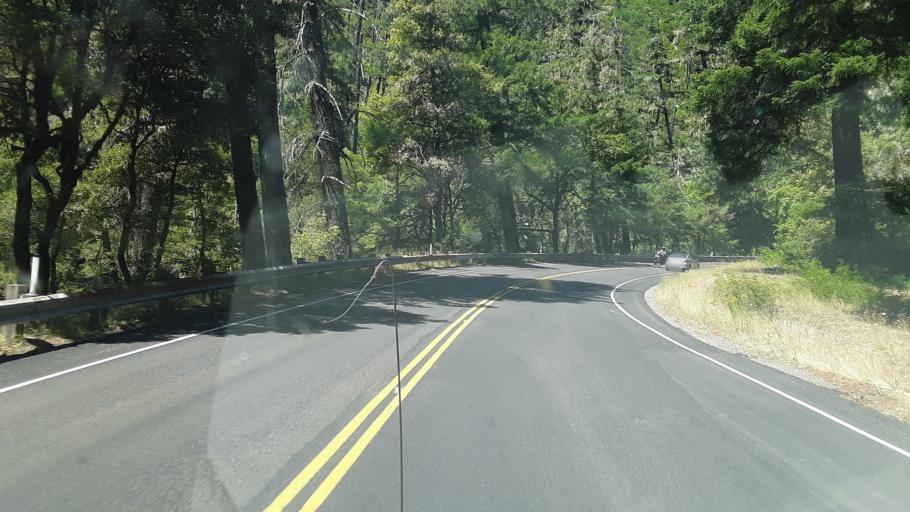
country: US
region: Oregon
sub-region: Josephine County
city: Cave Junction
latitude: 41.8819
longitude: -123.8273
